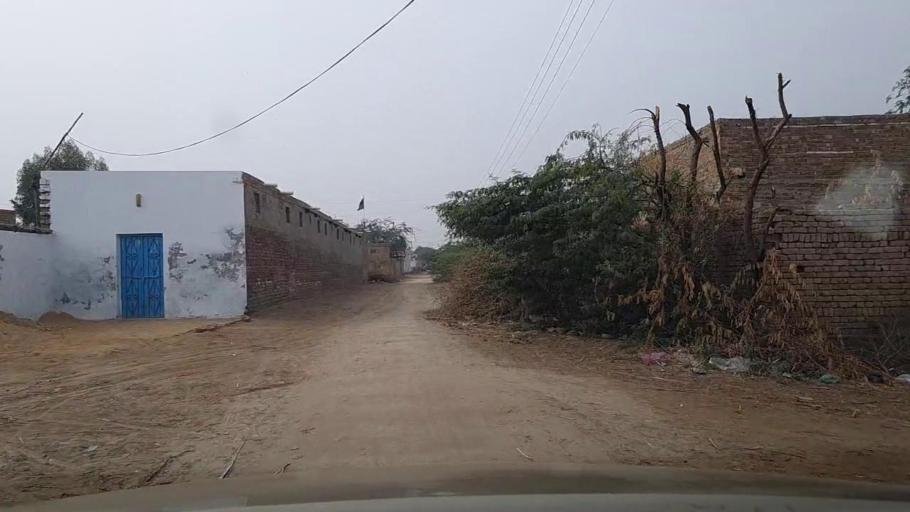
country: PK
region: Sindh
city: Sanghar
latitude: 26.1180
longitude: 68.8912
